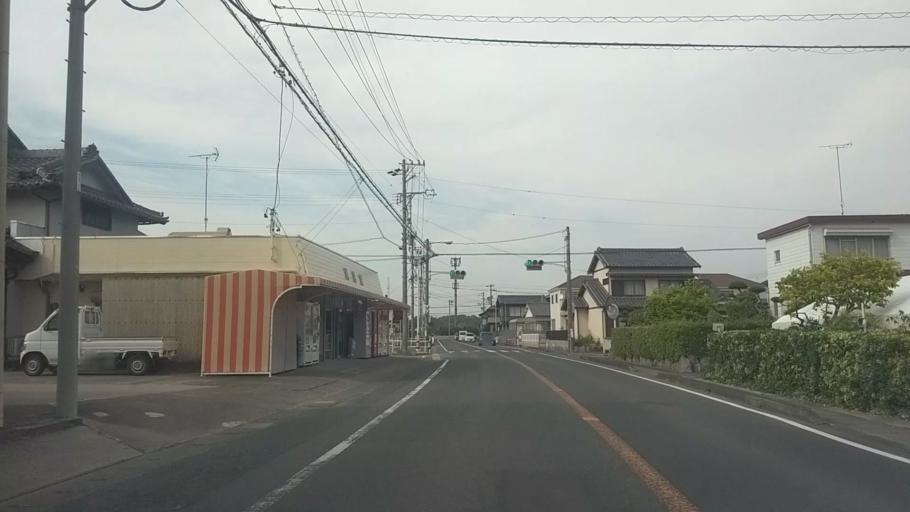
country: JP
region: Shizuoka
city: Kosai-shi
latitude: 34.7275
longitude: 137.6323
